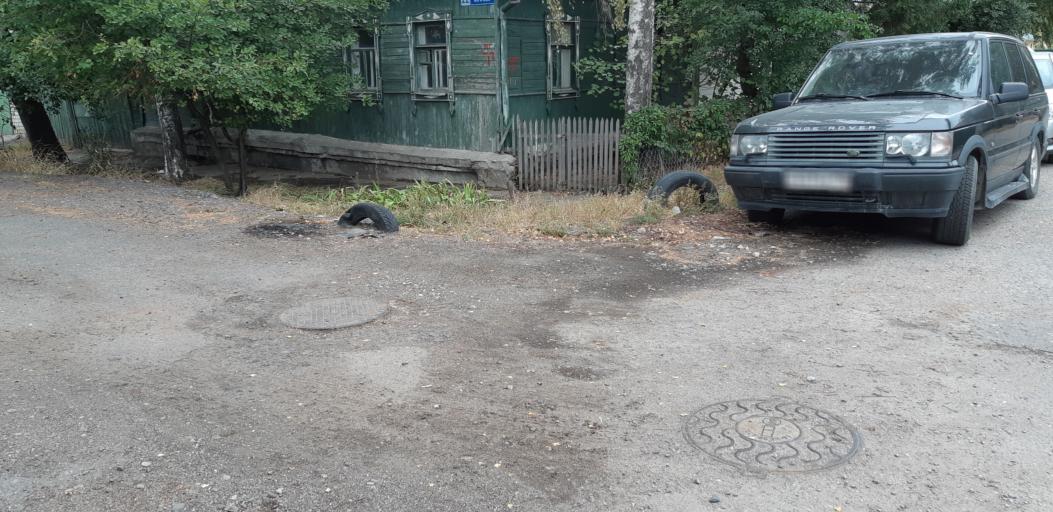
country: RU
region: Voronezj
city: Voronezh
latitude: 51.6601
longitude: 39.1657
